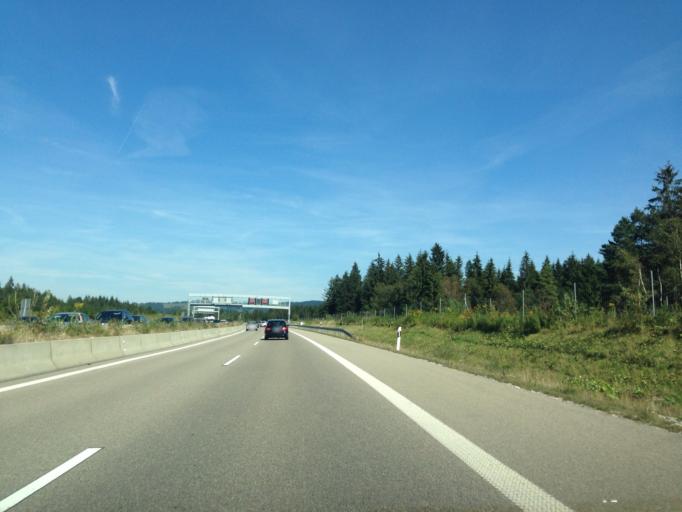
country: DE
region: Bavaria
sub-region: Swabia
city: Fuessen
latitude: 47.5802
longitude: 10.6623
